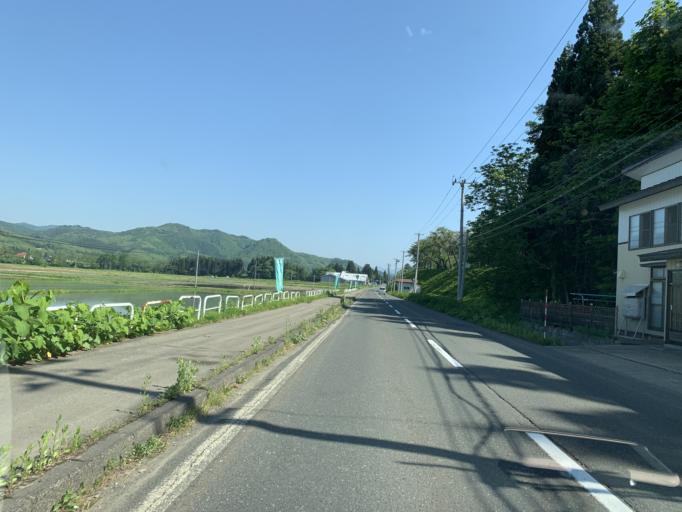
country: JP
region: Akita
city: Yokotemachi
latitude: 39.4053
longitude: 140.7532
